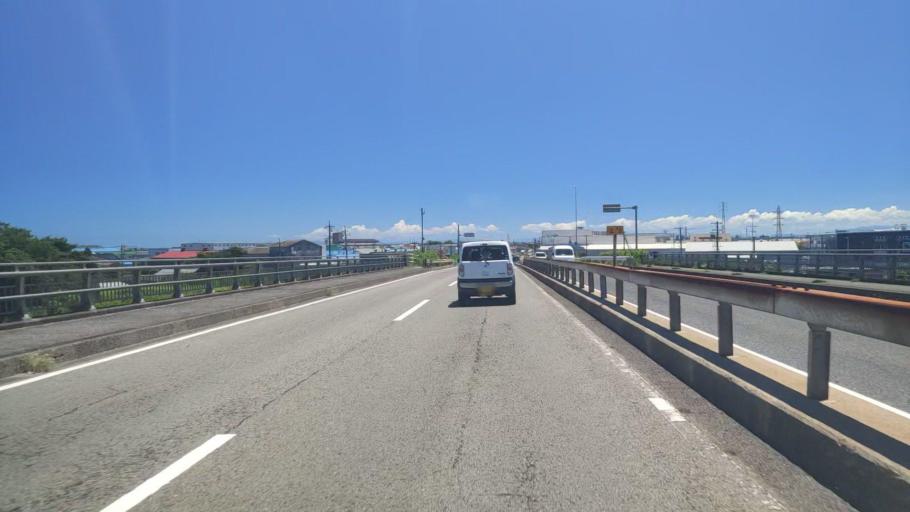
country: JP
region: Mie
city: Suzuka
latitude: 34.9067
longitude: 136.6055
